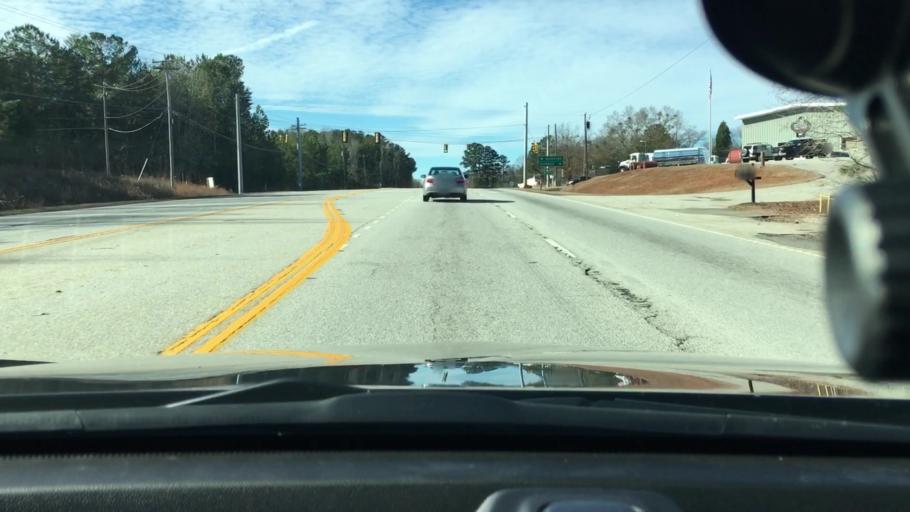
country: US
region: South Carolina
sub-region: Spartanburg County
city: Pacolet
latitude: 34.9254
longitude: -81.8361
